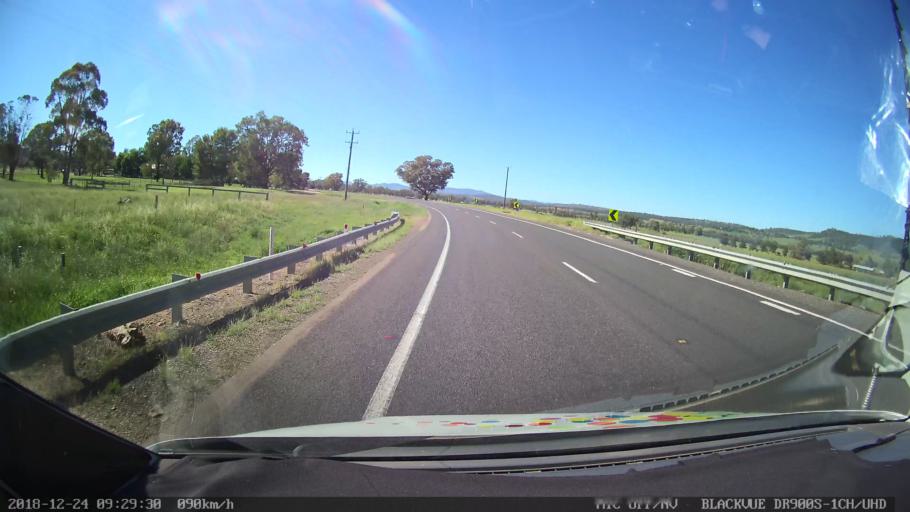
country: AU
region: New South Wales
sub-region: Liverpool Plains
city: Quirindi
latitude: -31.5510
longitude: 150.6920
